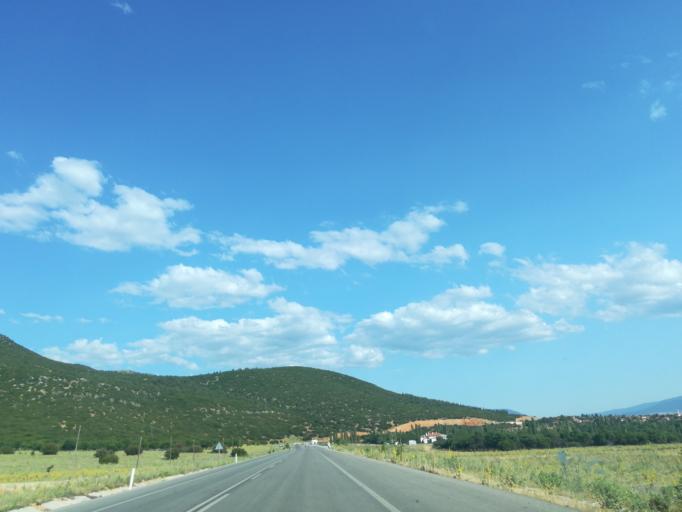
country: TR
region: Denizli
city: Ishakli
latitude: 38.1640
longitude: 30.0760
